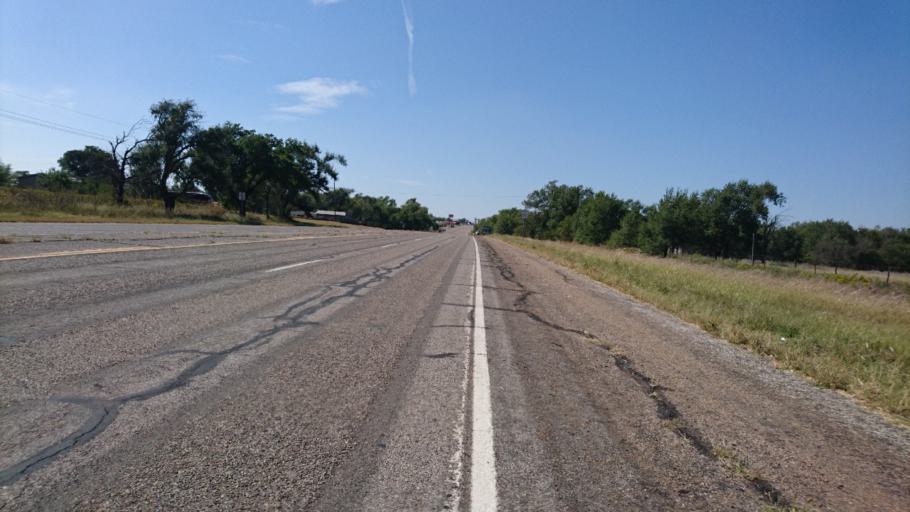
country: US
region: Texas
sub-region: Wheeler County
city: Shamrock
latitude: 35.2267
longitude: -100.2320
